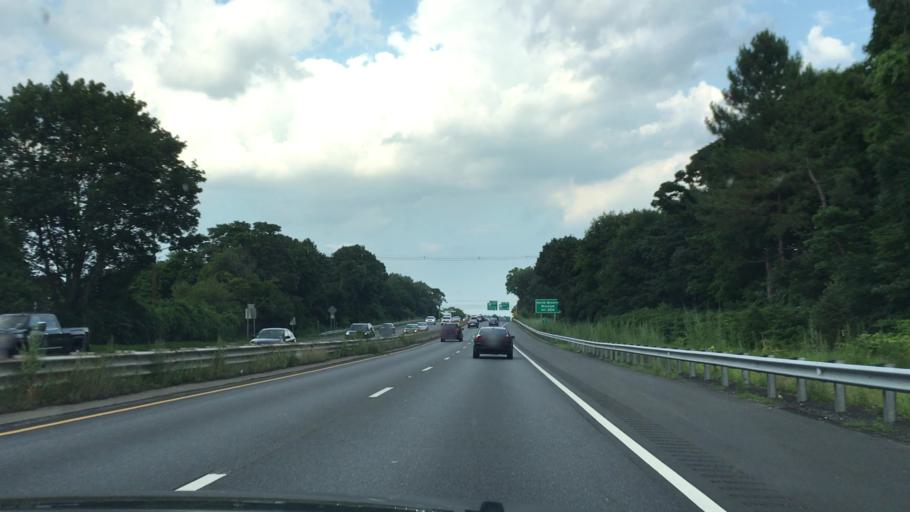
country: US
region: Massachusetts
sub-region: Essex County
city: Beverly
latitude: 42.5737
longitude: -70.8988
